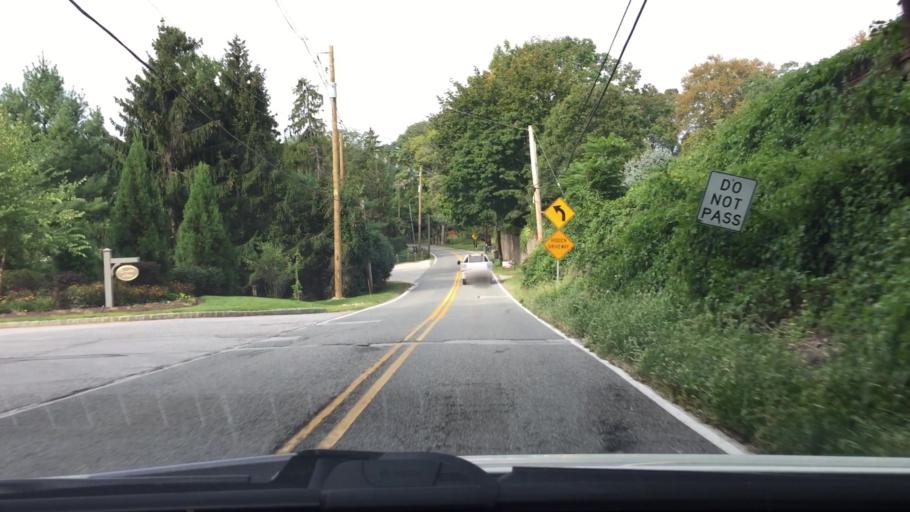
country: US
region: Pennsylvania
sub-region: Delaware County
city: Radnor
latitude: 40.0293
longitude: -75.3682
